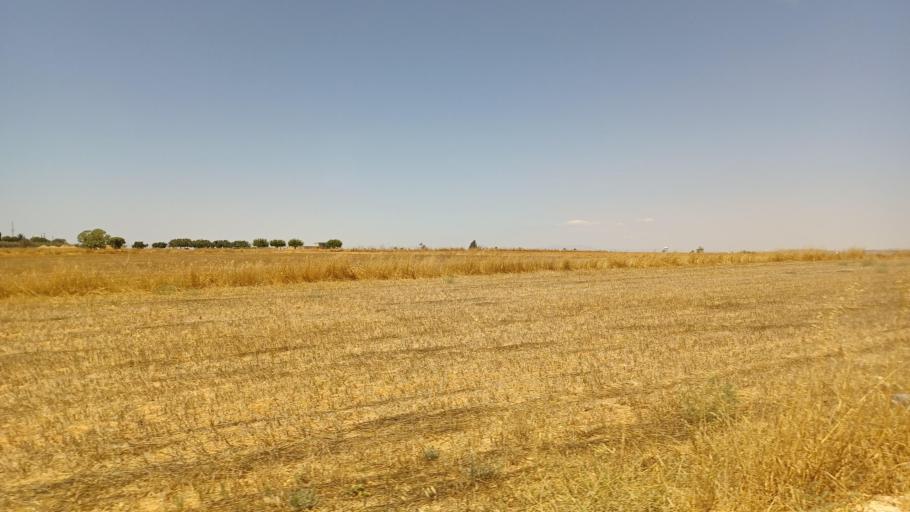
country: CY
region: Larnaka
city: Xylotymbou
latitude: 35.0132
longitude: 33.7274
